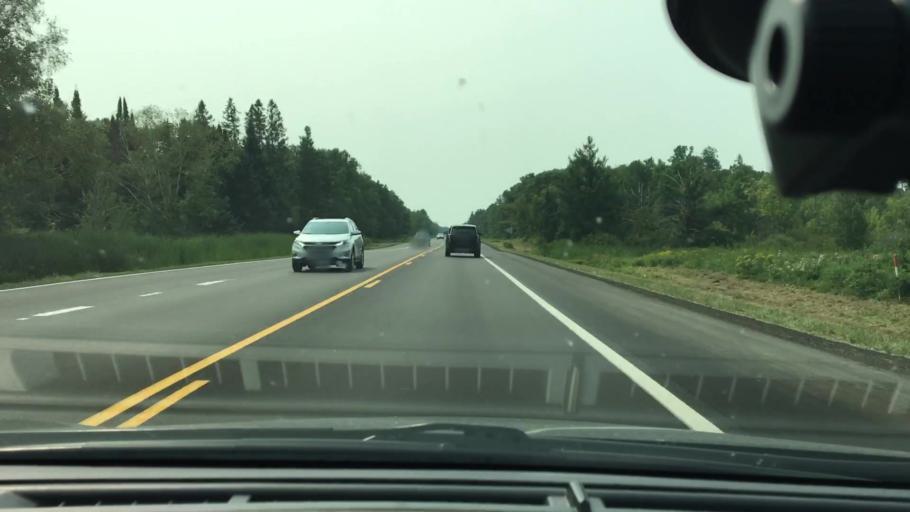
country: US
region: Minnesota
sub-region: Crow Wing County
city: Brainerd
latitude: 46.4554
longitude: -94.1723
